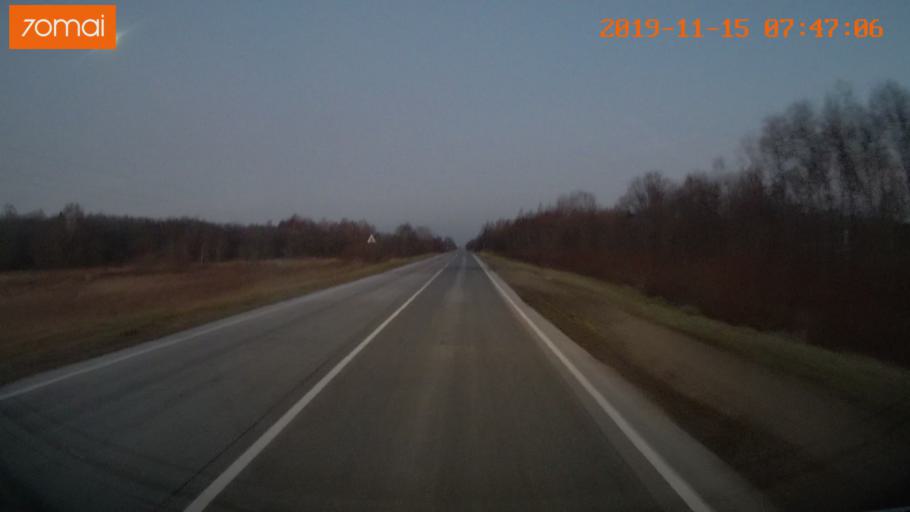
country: RU
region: Vologda
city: Sheksna
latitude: 58.8382
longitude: 38.2673
